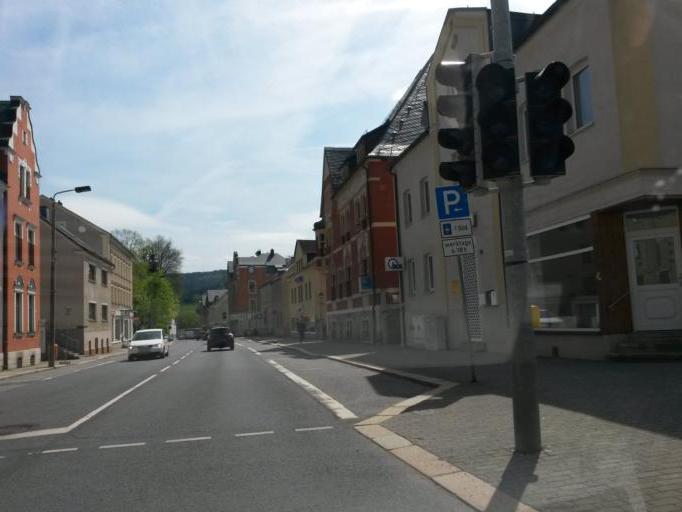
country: DE
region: Saxony
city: Klingenthal
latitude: 50.3597
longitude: 12.4700
